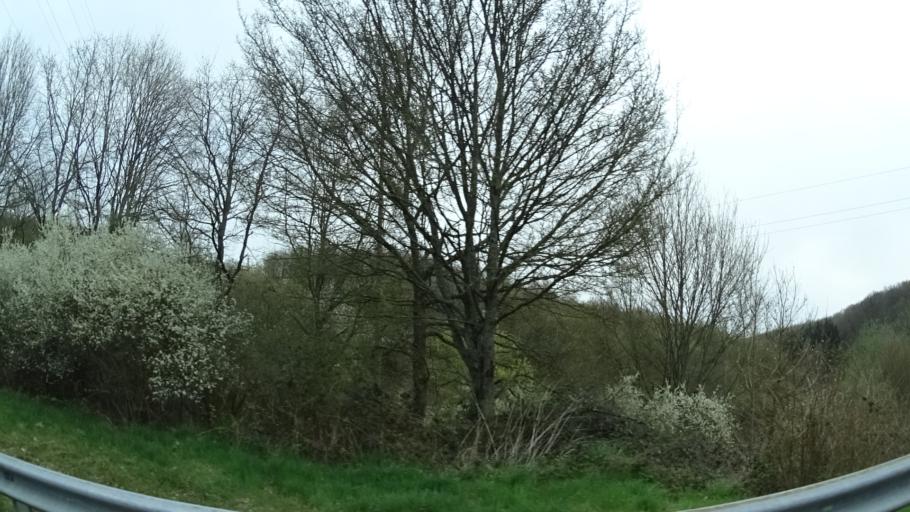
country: DE
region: Rheinland-Pfalz
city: Heinzenberg
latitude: 49.8066
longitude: 7.4757
